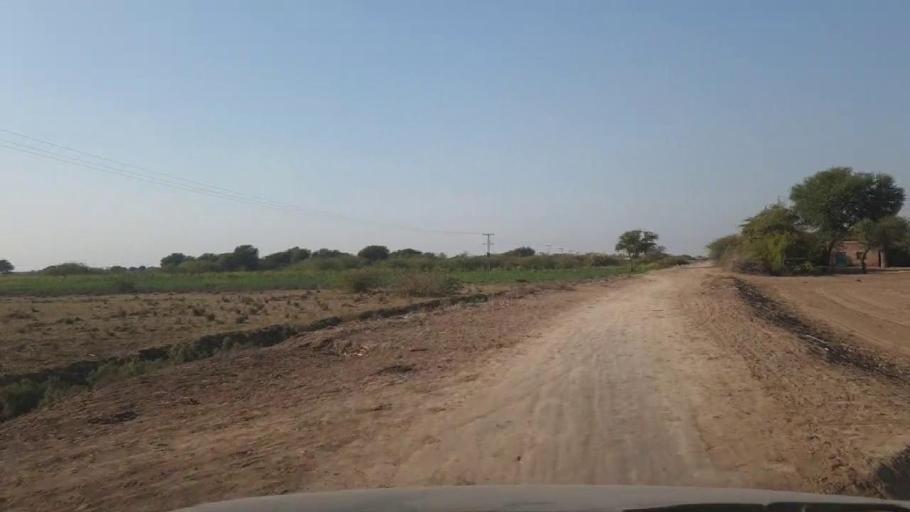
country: PK
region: Sindh
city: Chambar
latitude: 25.3022
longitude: 68.8605
